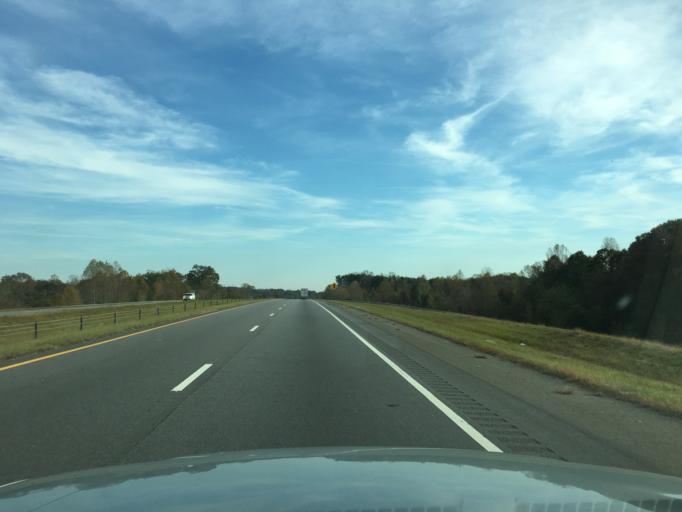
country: US
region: North Carolina
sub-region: Catawba County
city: Newton
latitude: 35.6354
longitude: -81.2976
